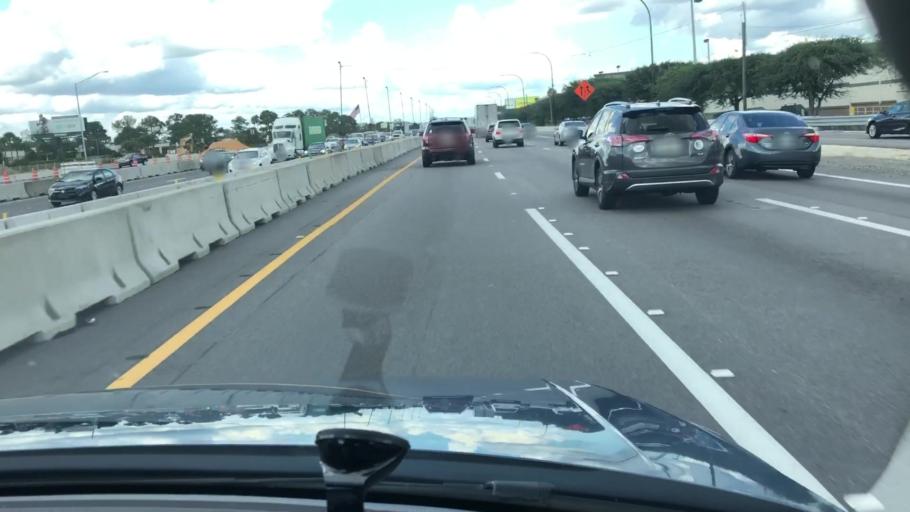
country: US
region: Florida
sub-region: Orange County
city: Oak Ridge
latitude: 28.4956
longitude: -81.4311
